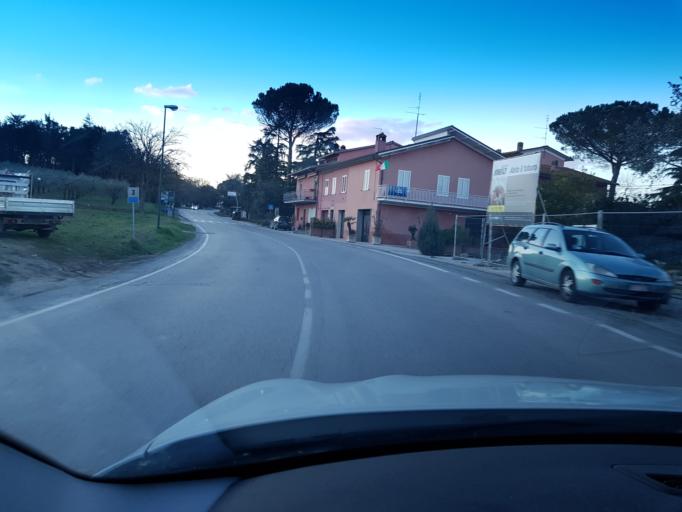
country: IT
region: Umbria
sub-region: Provincia di Perugia
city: Torgiano
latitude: 43.0275
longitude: 12.4443
